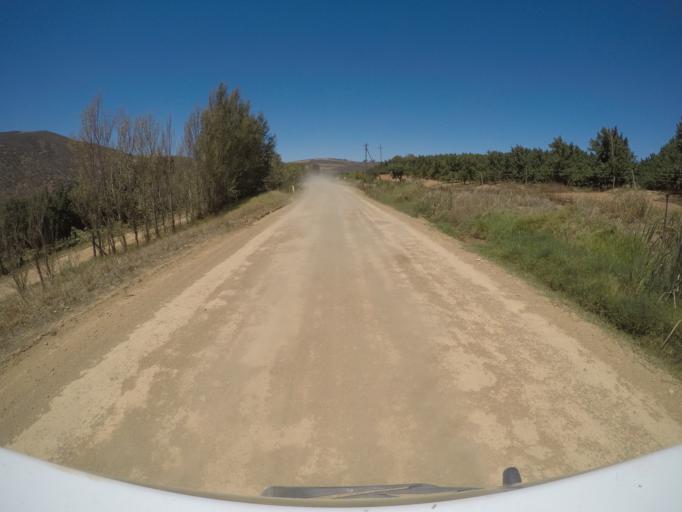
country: ZA
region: Western Cape
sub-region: Overberg District Municipality
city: Grabouw
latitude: -34.1094
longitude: 19.2125
